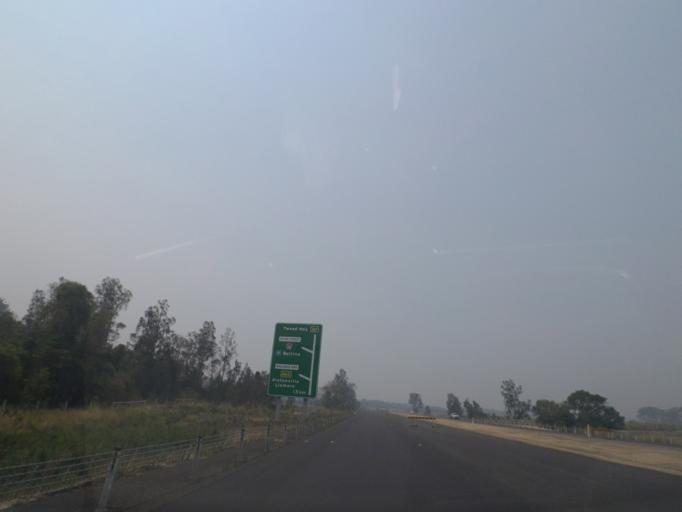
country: AU
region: New South Wales
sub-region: Ballina
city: Ballina
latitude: -28.8759
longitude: 153.4887
